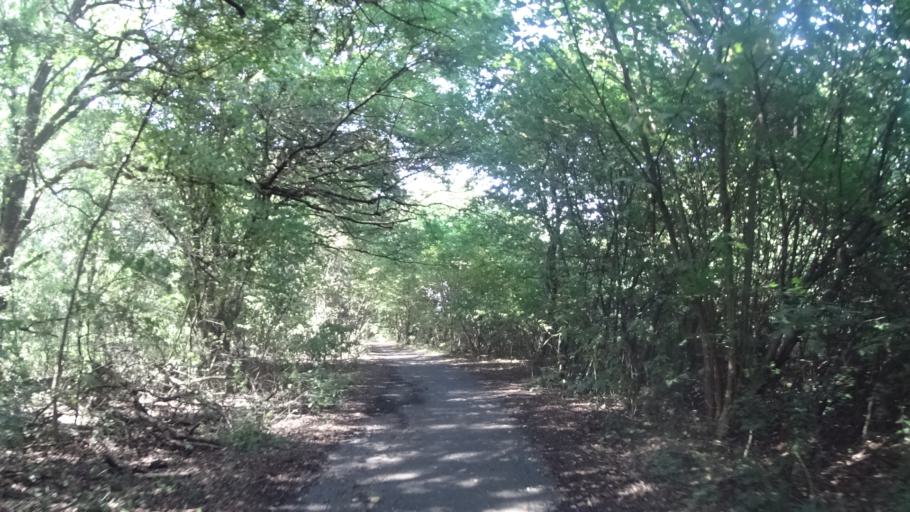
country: AT
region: Lower Austria
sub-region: Politischer Bezirk Ganserndorf
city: Angern an der March
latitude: 48.3529
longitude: 16.8865
